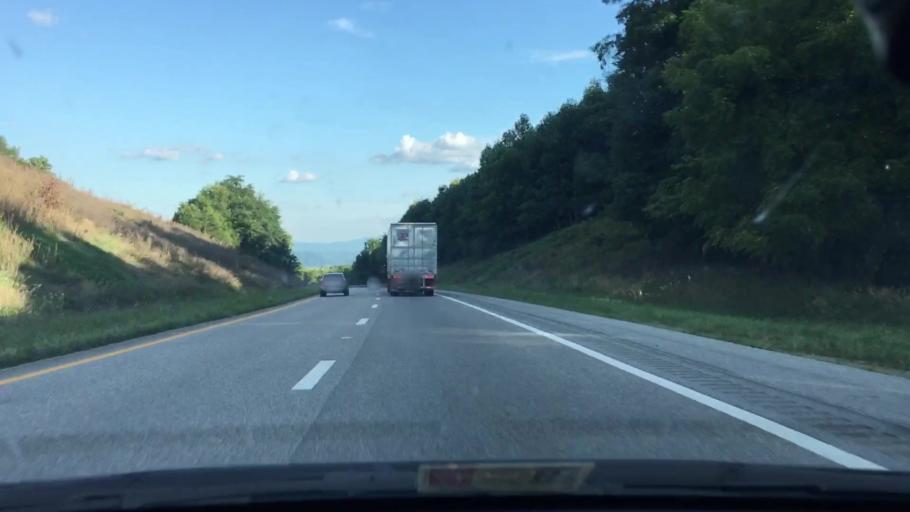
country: US
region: Virginia
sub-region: City of Lexington
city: Lexington
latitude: 37.8891
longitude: -79.5626
